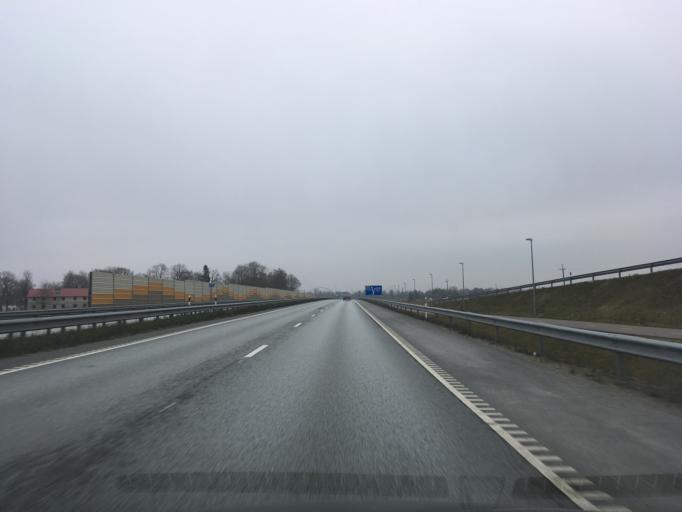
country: EE
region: Ida-Virumaa
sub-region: Johvi vald
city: Johvi
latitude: 59.3747
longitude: 27.3798
